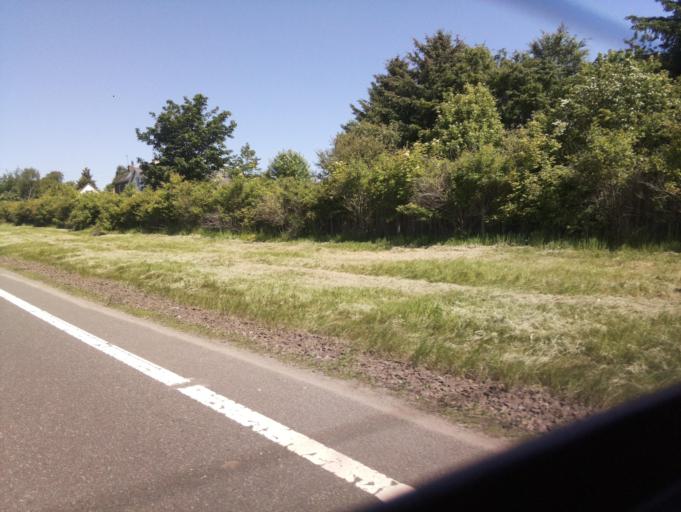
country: GB
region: Scotland
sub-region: Fife
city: Pathhead
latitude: 55.7911
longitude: -2.9638
